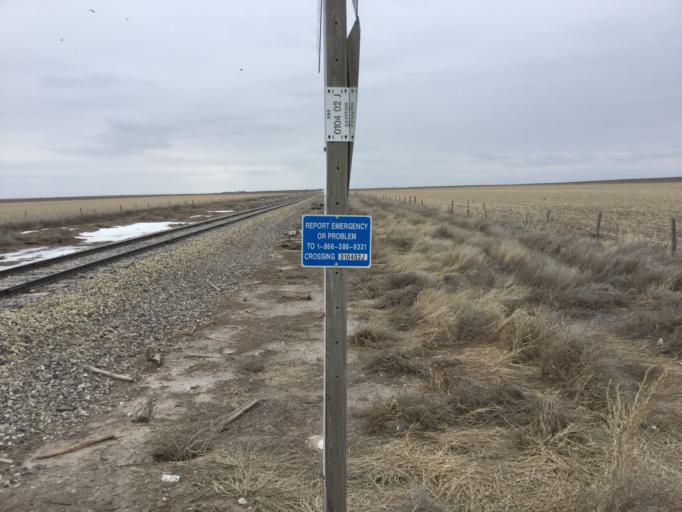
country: US
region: Kansas
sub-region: Scott County
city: Scott City
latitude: 38.4848
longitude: -100.7049
